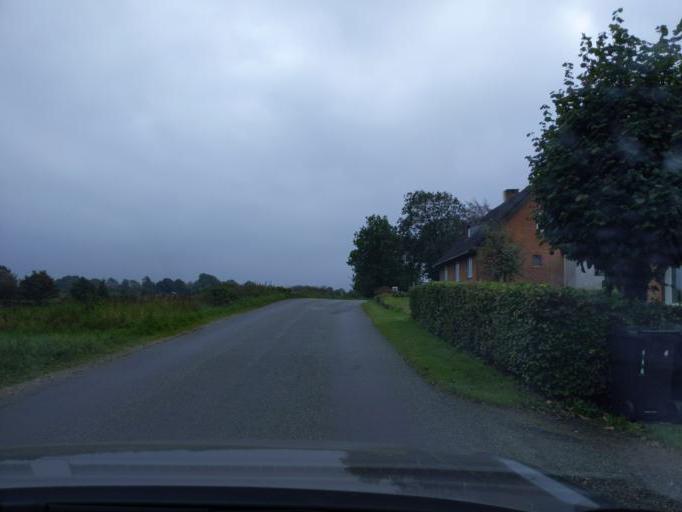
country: DK
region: Central Jutland
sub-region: Viborg Kommune
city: Viborg
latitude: 56.3675
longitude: 9.2960
